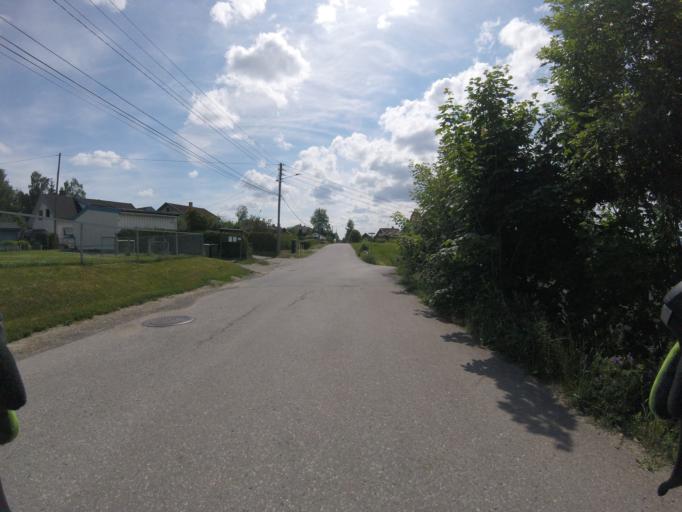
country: NO
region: Akershus
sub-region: Skedsmo
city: Lillestrom
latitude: 59.9841
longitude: 11.0488
